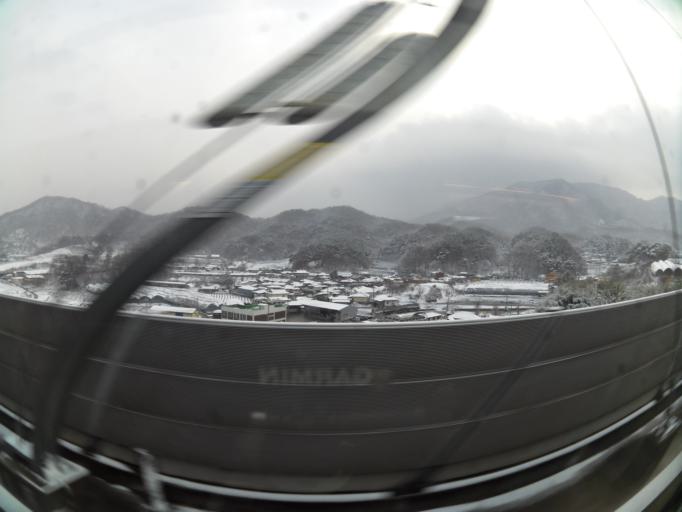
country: KR
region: Chungcheongbuk-do
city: Okcheon
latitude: 36.2602
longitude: 127.5849
